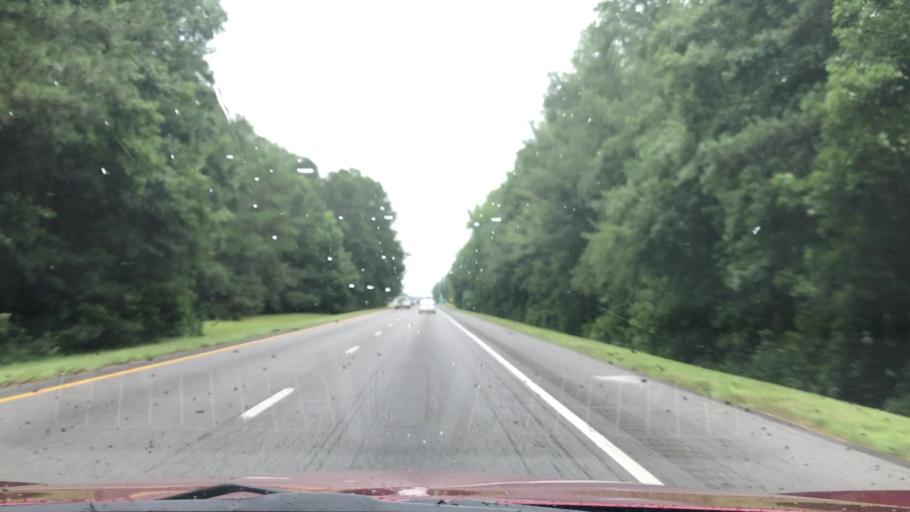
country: US
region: South Carolina
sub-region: Dorchester County
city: Ridgeville
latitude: 33.1404
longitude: -80.3176
